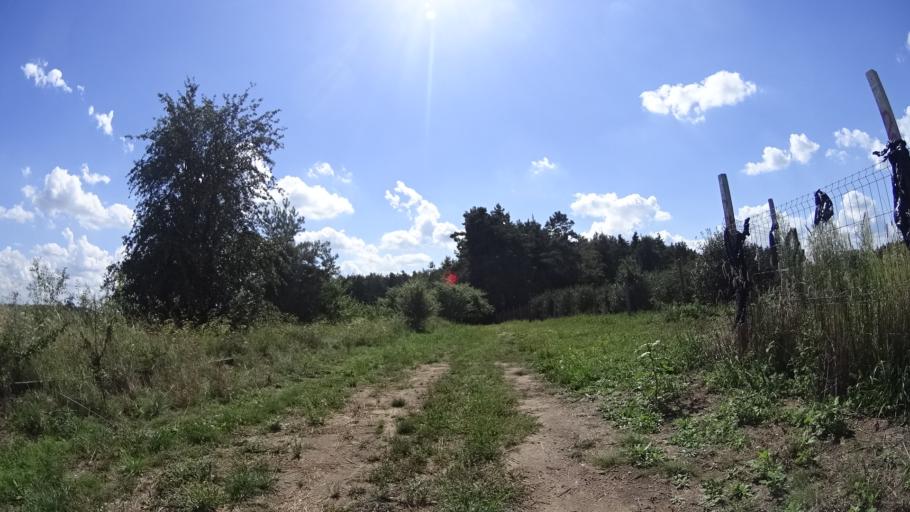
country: PL
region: Masovian Voivodeship
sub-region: Powiat grojecki
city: Mogielnica
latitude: 51.6783
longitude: 20.7518
